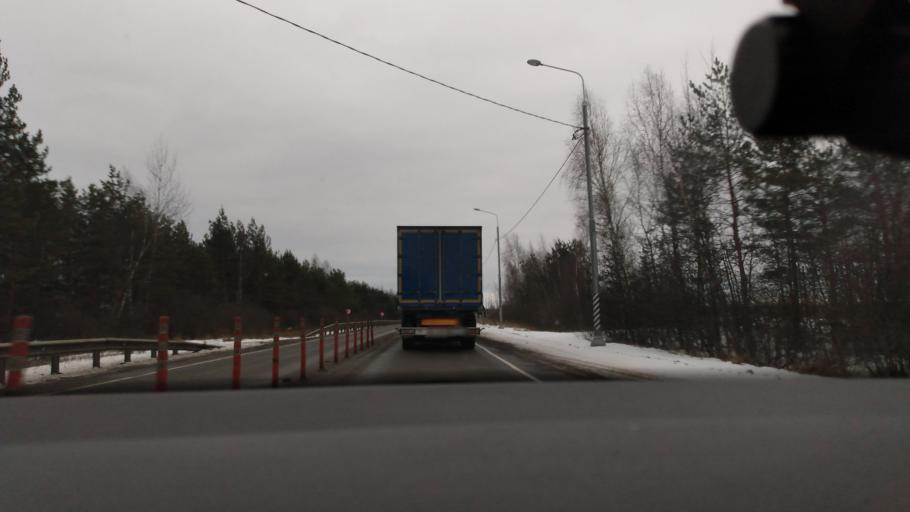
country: RU
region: Moskovskaya
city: Yegor'yevsk
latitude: 55.4468
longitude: 39.0118
